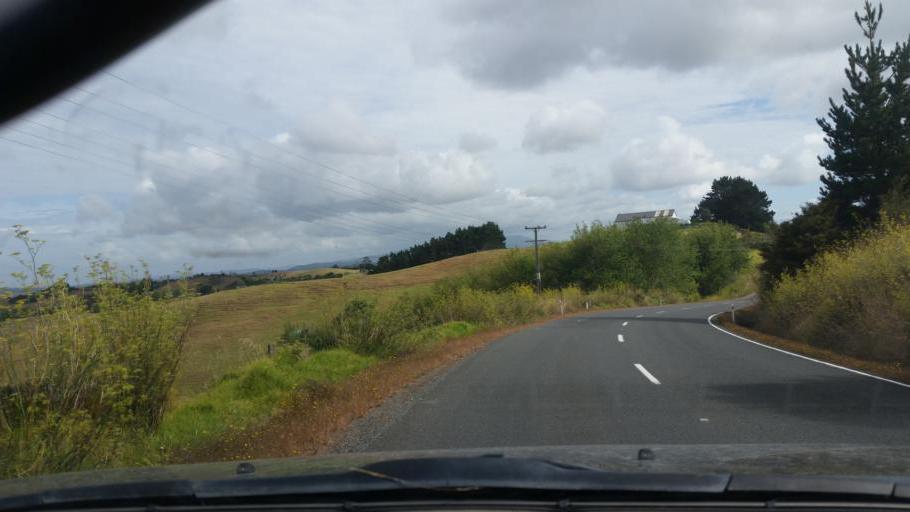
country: NZ
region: Northland
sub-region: Kaipara District
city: Dargaville
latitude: -35.9560
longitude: 173.9225
